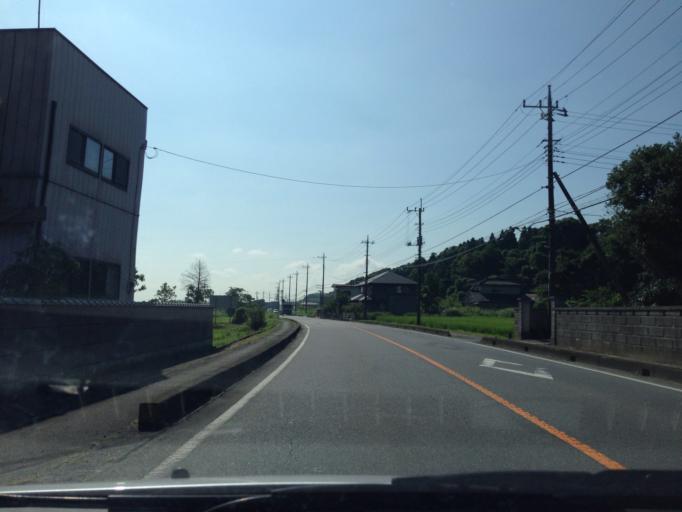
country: JP
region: Ibaraki
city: Ami
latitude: 36.0436
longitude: 140.2247
